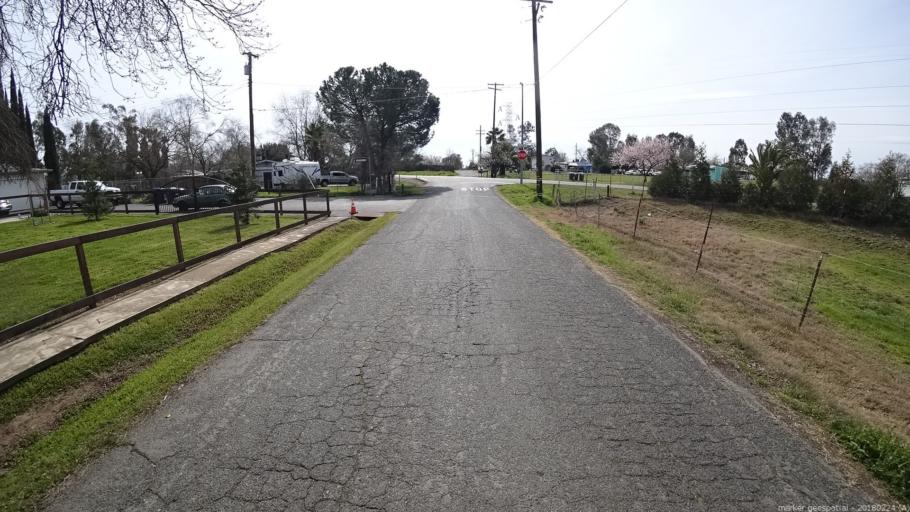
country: US
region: California
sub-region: Sacramento County
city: Rio Linda
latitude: 38.6879
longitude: -121.4708
